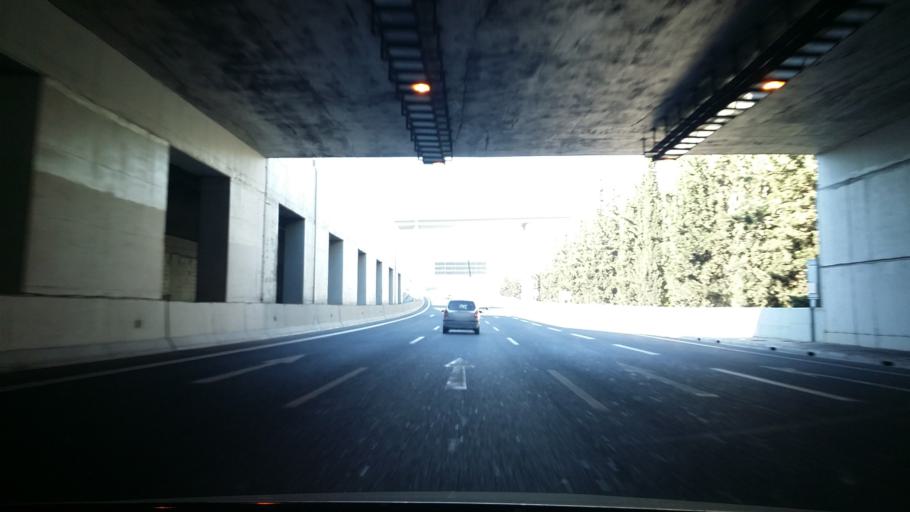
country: GR
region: Attica
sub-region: Nomarchia Dytikis Attikis
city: Zefyri
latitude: 38.0679
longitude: 23.7284
